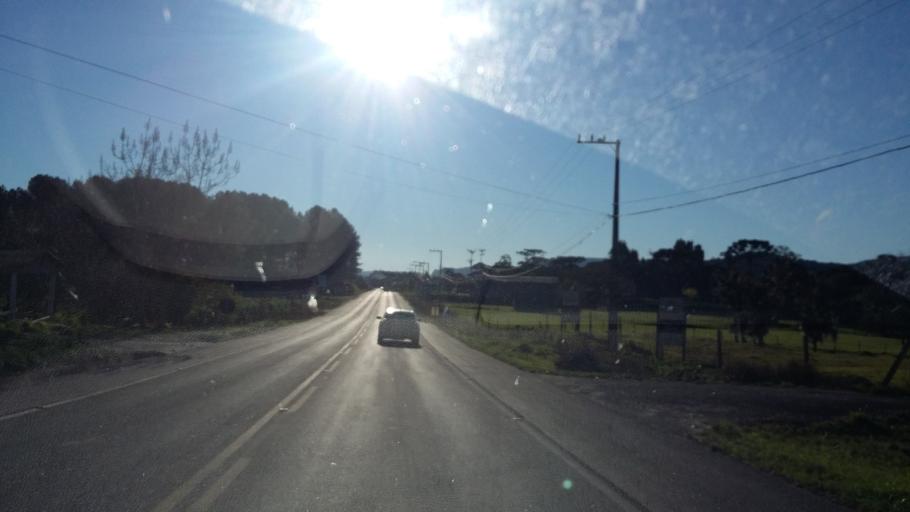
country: BR
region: Santa Catarina
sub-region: Lauro Muller
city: Lauro Muller
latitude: -27.9998
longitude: -49.5507
